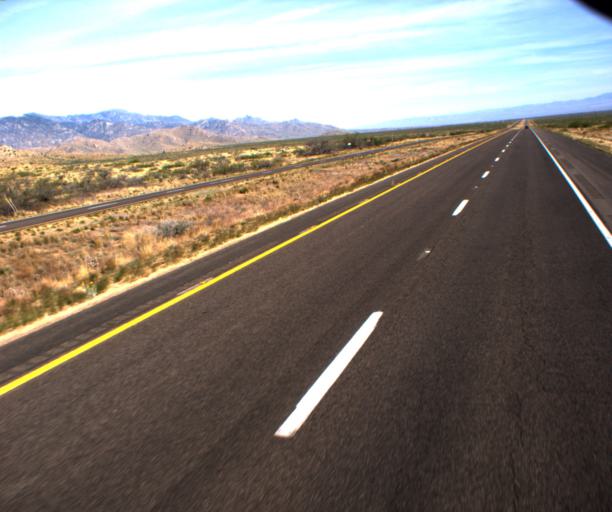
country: US
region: Arizona
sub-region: Graham County
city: Swift Trail Junction
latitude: 32.5315
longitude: -109.6744
